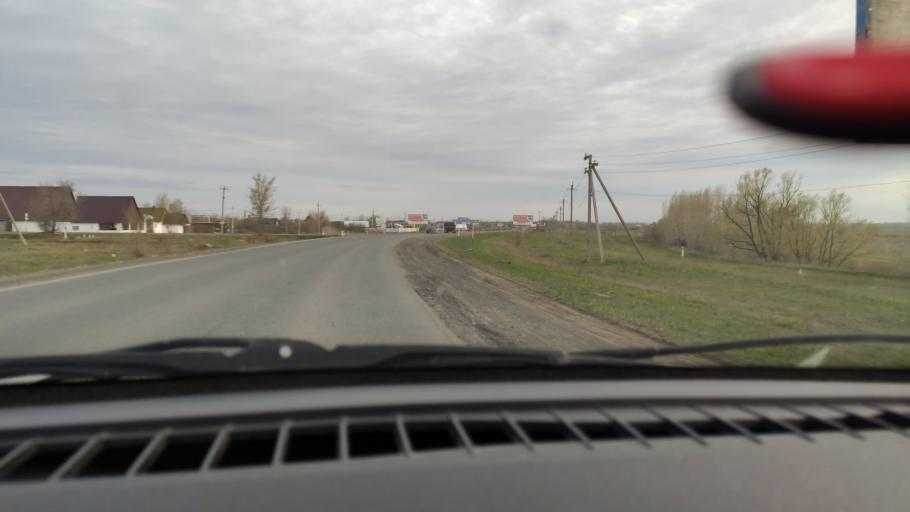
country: RU
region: Orenburg
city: Tatarskaya Kargala
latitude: 51.9036
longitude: 55.1699
